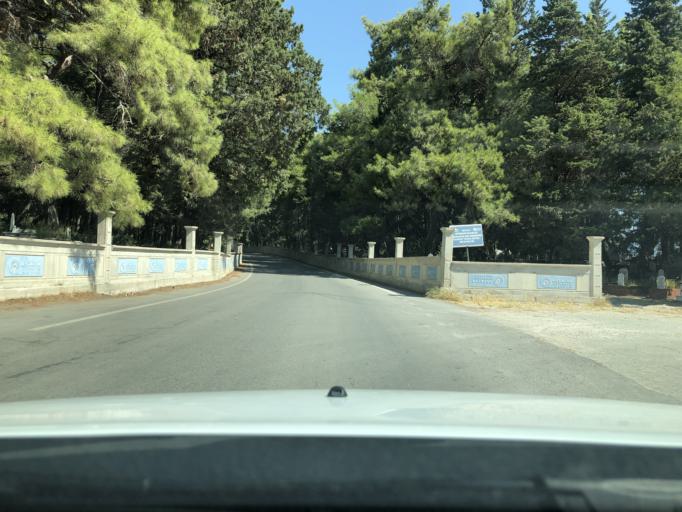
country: TR
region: Antalya
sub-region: Manavgat
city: Manavgat
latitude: 36.8147
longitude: 31.4889
